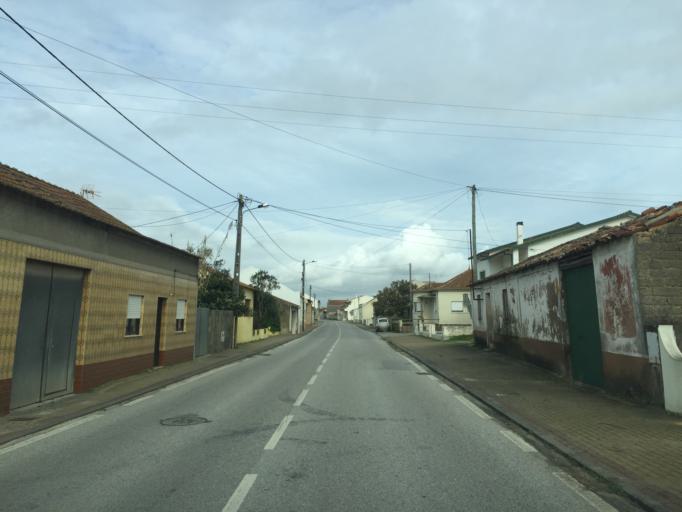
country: PT
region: Coimbra
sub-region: Figueira da Foz
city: Lavos
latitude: 40.0574
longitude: -8.8142
